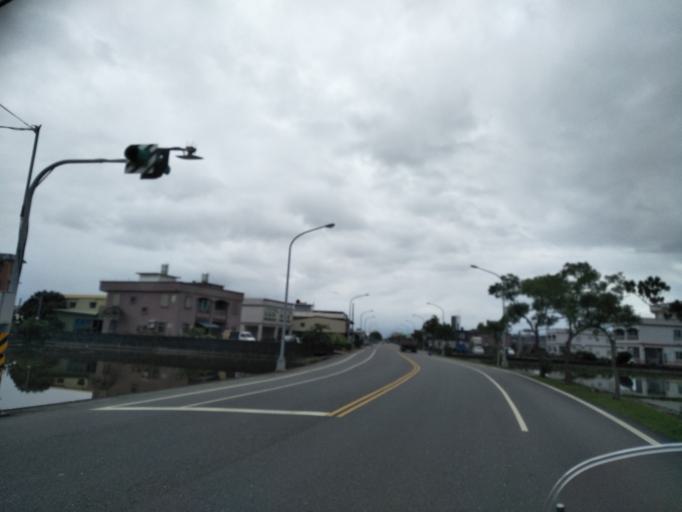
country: TW
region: Taiwan
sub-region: Yilan
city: Yilan
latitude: 24.7929
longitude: 121.7846
